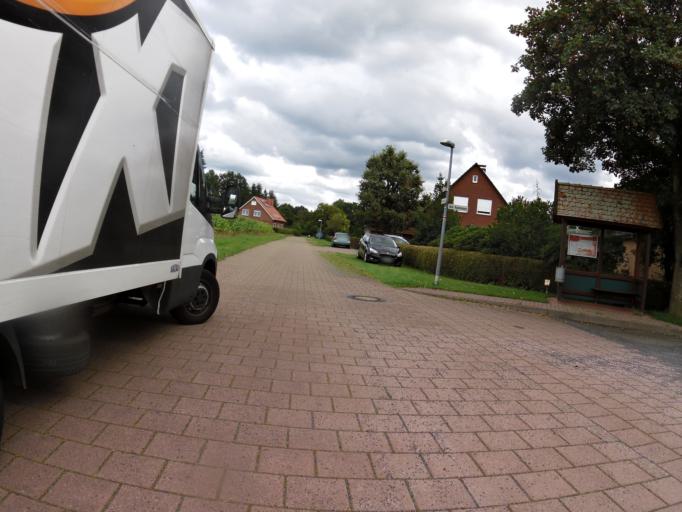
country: DE
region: Lower Saxony
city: Kohlen
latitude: 53.5091
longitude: 8.8710
